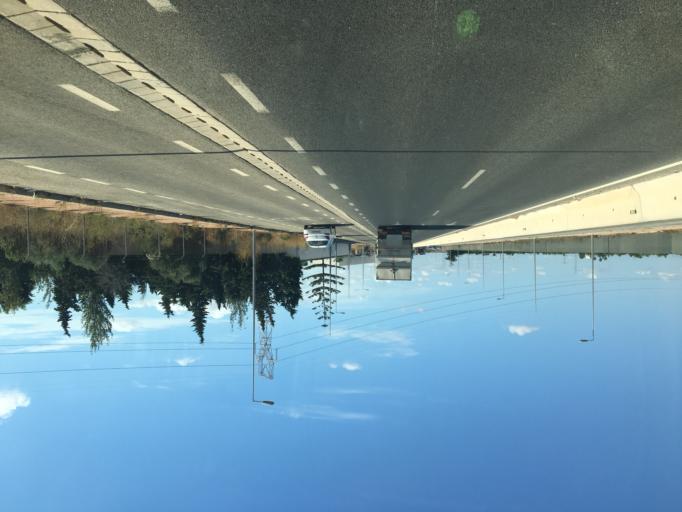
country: ES
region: Murcia
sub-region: Murcia
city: Cartagena
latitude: 37.6501
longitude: -0.9840
